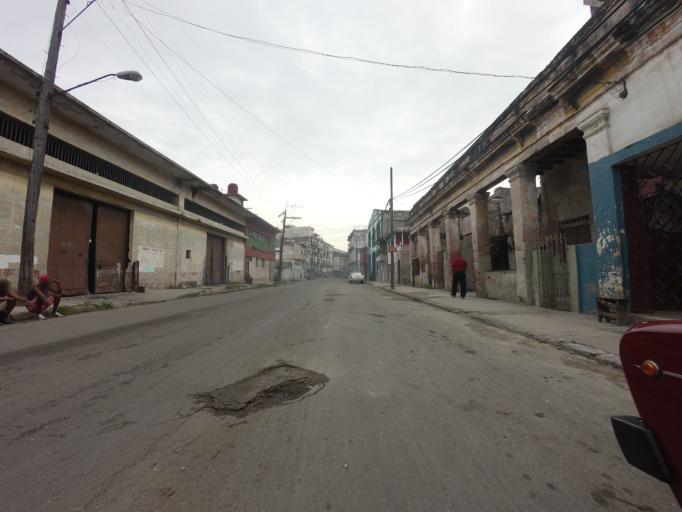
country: CU
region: La Habana
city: Centro Habana
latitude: 23.1230
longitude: -82.3679
